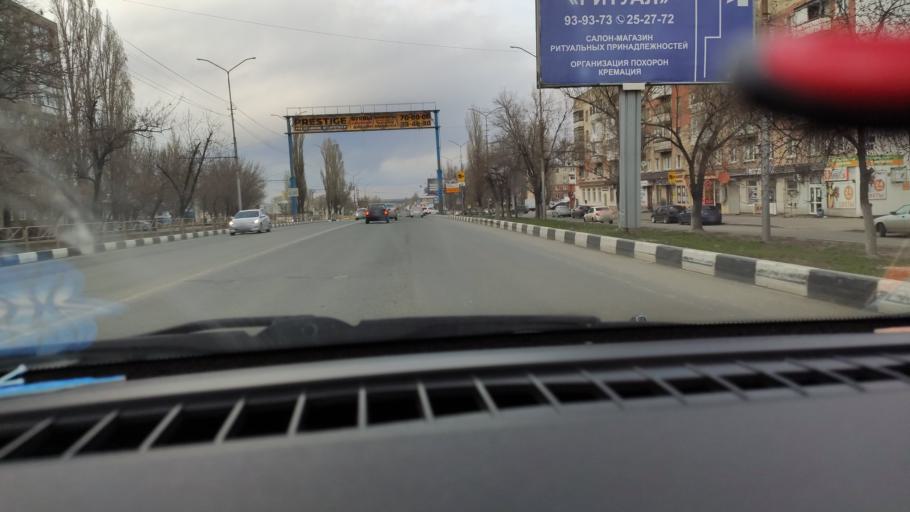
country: RU
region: Saratov
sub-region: Saratovskiy Rayon
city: Saratov
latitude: 51.6030
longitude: 45.9688
